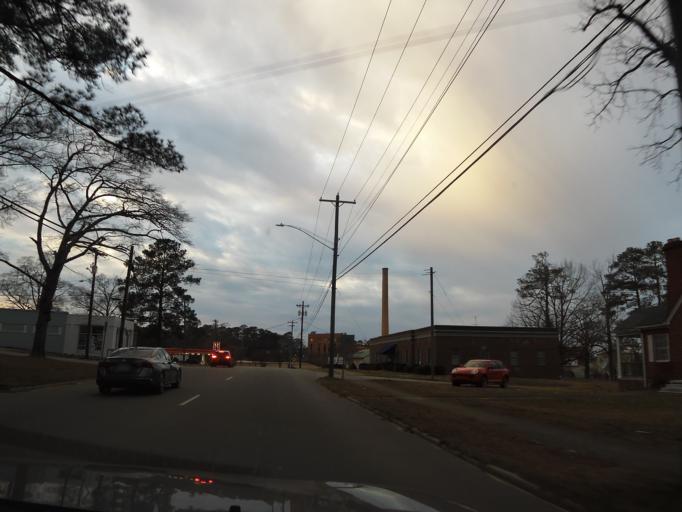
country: US
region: North Carolina
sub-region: Nash County
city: Rocky Mount
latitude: 35.9504
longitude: -77.8167
